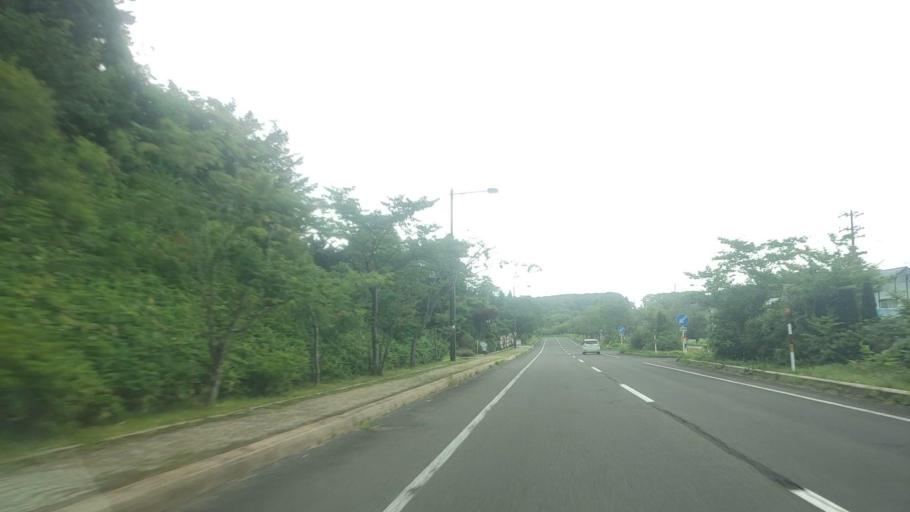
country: JP
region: Hokkaido
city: Shiraoi
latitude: 42.4661
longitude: 141.1685
